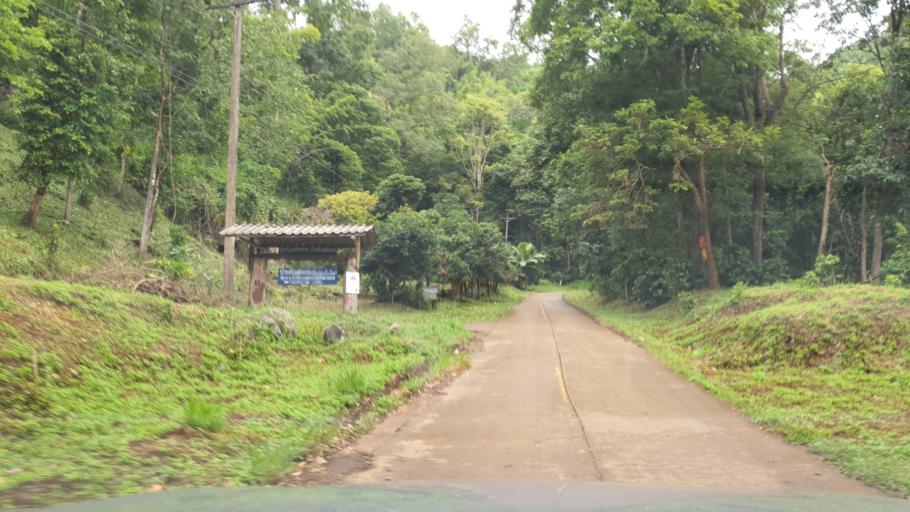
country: TH
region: Chiang Mai
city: Mae Taeng
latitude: 19.2304
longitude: 98.9231
